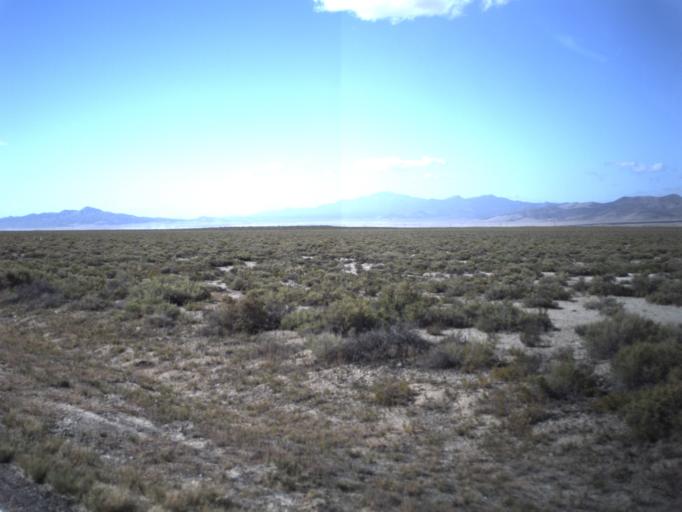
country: US
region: Utah
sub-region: Beaver County
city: Milford
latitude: 38.7087
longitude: -112.9704
